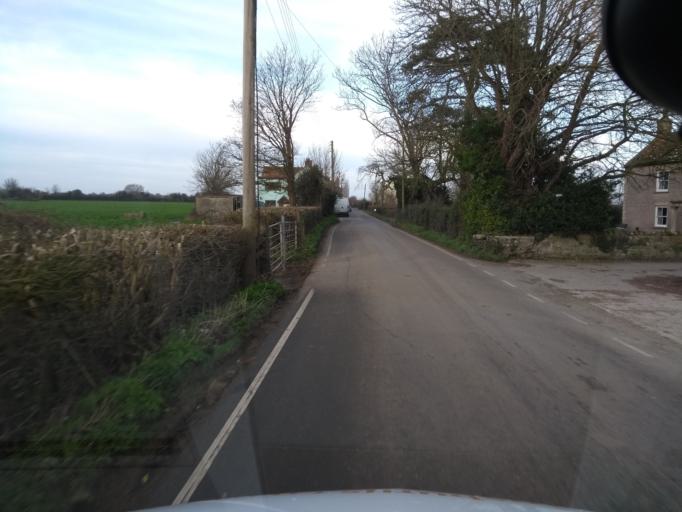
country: GB
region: England
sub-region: Somerset
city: Burnham-on-Sea
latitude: 51.2593
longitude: -2.9743
